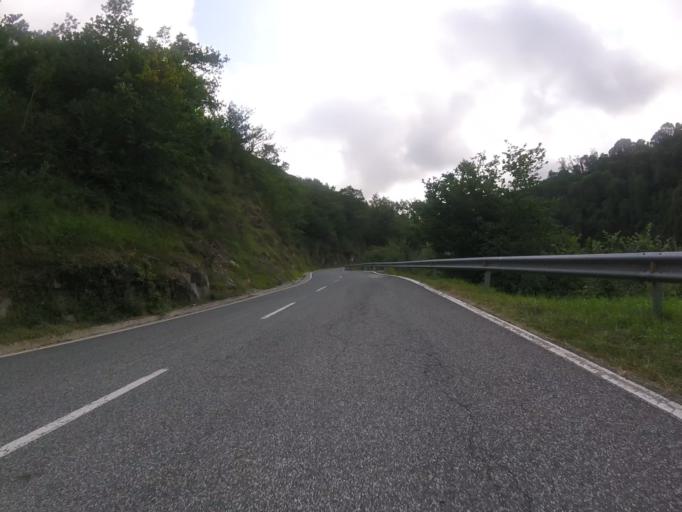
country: ES
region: Navarre
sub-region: Provincia de Navarra
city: Eratsun
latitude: 43.0870
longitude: -1.8005
